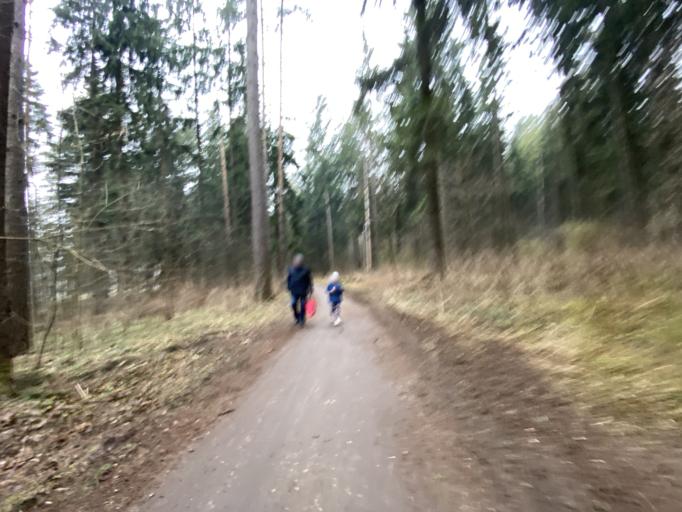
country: BY
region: Minsk
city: Borovlyany
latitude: 53.9453
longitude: 27.6605
